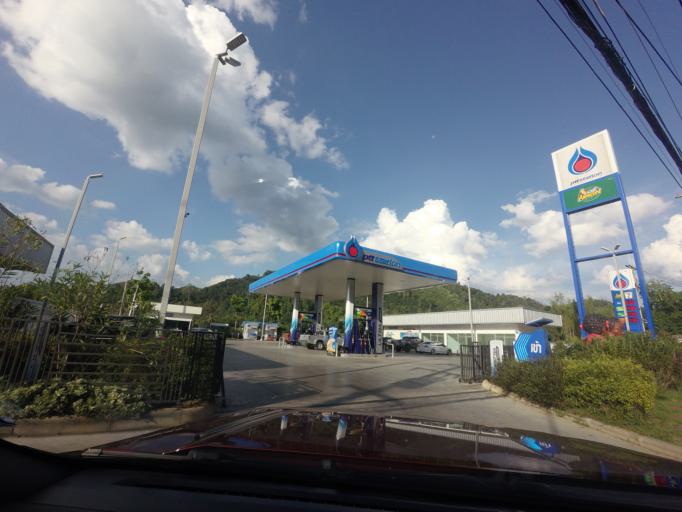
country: TH
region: Yala
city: Than To
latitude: 6.1604
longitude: 101.1883
